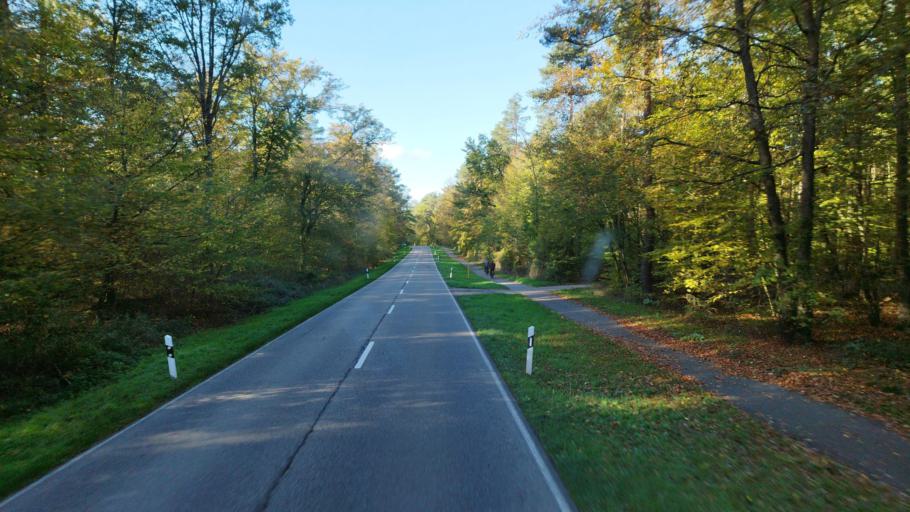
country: DE
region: Rheinland-Pfalz
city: Jockgrim
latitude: 49.0972
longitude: 8.2593
